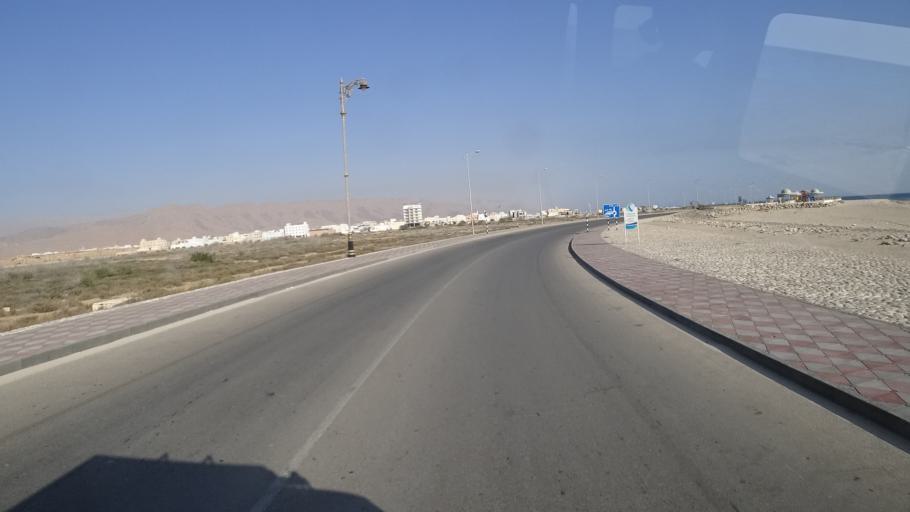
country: OM
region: Ash Sharqiyah
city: Sur
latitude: 22.5984
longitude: 59.4867
